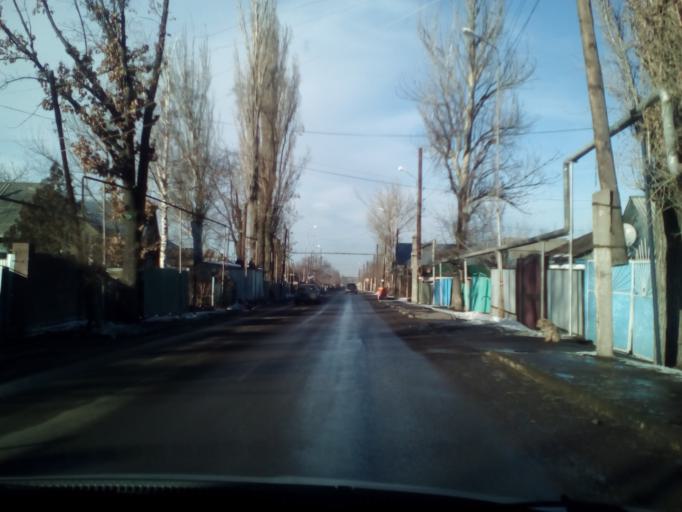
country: KZ
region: Almaty Oblysy
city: Burunday
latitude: 43.1654
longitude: 76.4170
